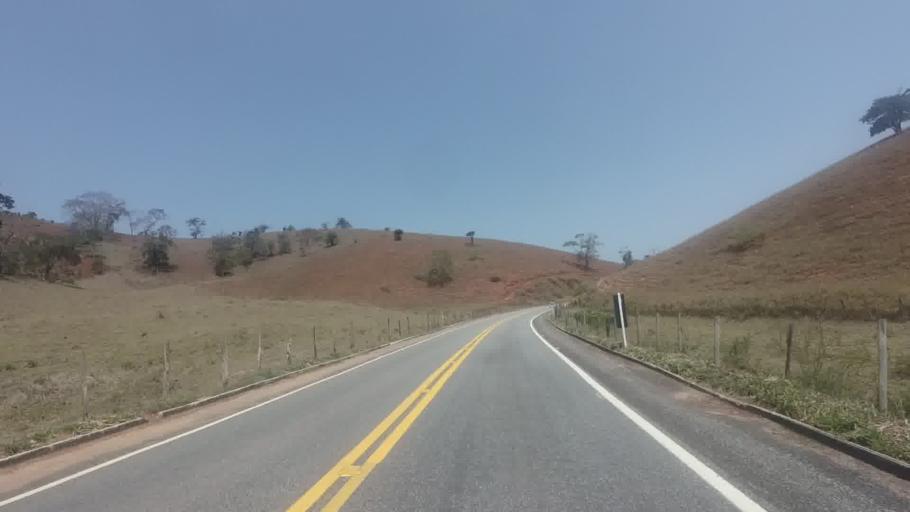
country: BR
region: Espirito Santo
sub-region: Jeronimo Monteiro
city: Jeronimo Monteiro
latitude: -20.8906
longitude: -41.2803
